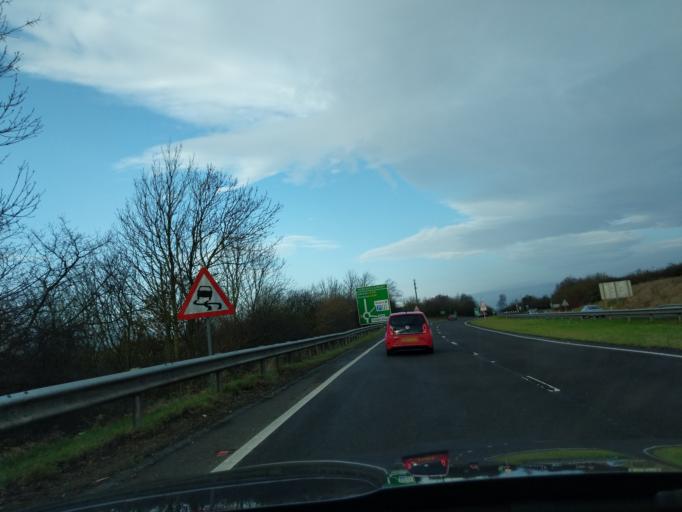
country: GB
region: England
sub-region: Northumberland
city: Ponteland
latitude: 55.0338
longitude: -1.7139
